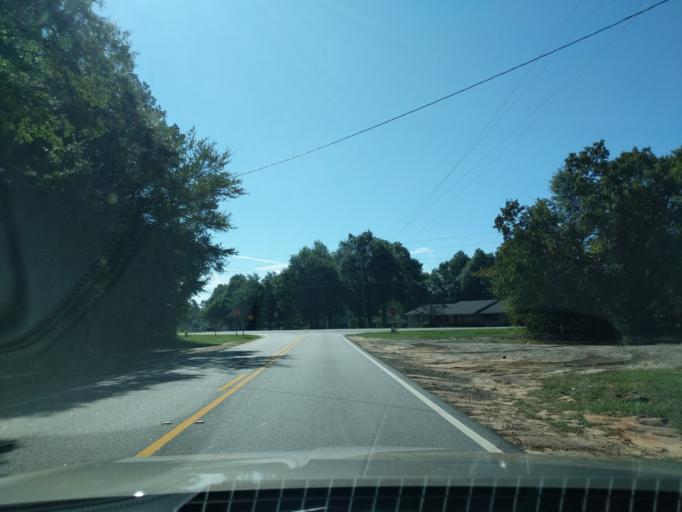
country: US
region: Georgia
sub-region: Richmond County
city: Hephzibah
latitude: 33.2574
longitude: -82.0073
